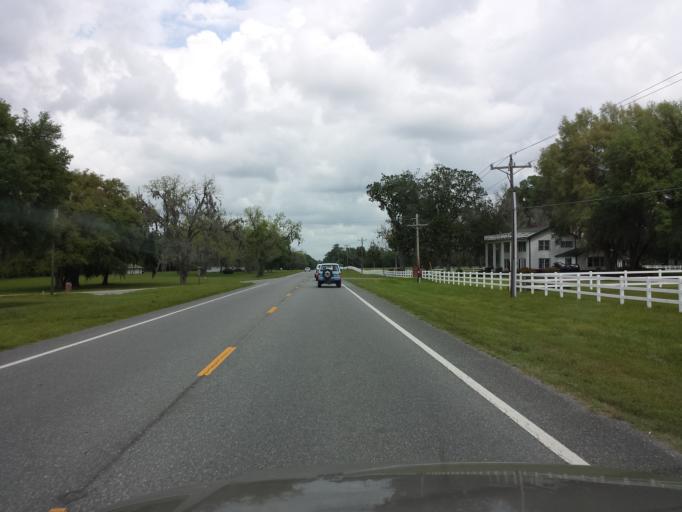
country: US
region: Florida
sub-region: Columbia County
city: Watertown
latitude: 30.0796
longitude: -82.6010
